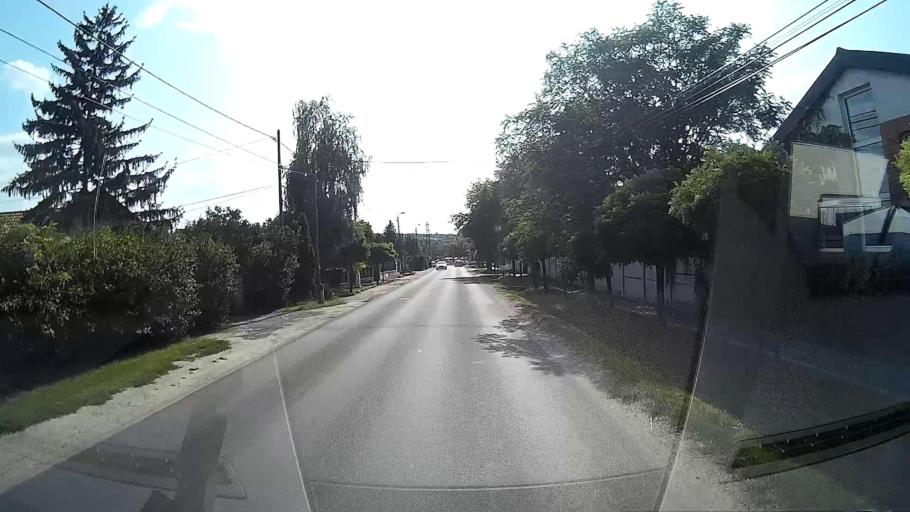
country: HU
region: Pest
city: Budakalasz
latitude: 47.6234
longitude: 19.0508
